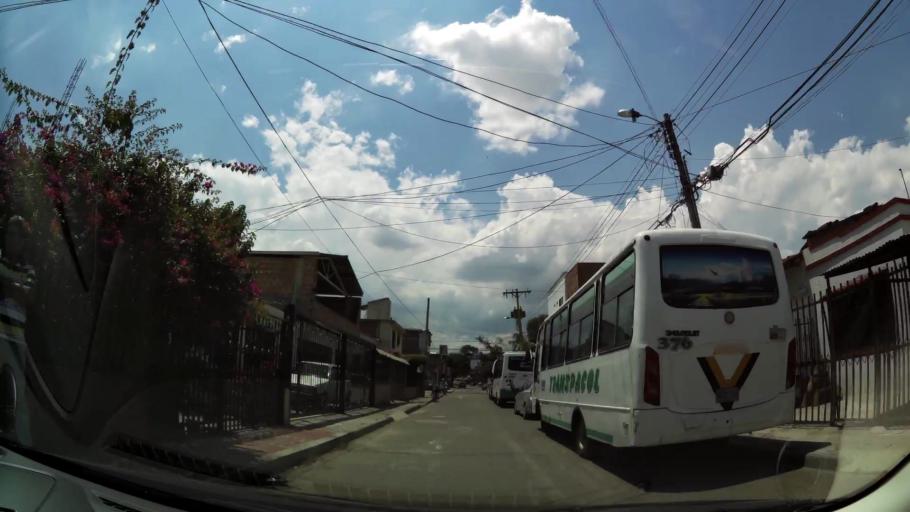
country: CO
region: Valle del Cauca
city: Cali
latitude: 3.4478
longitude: -76.5010
